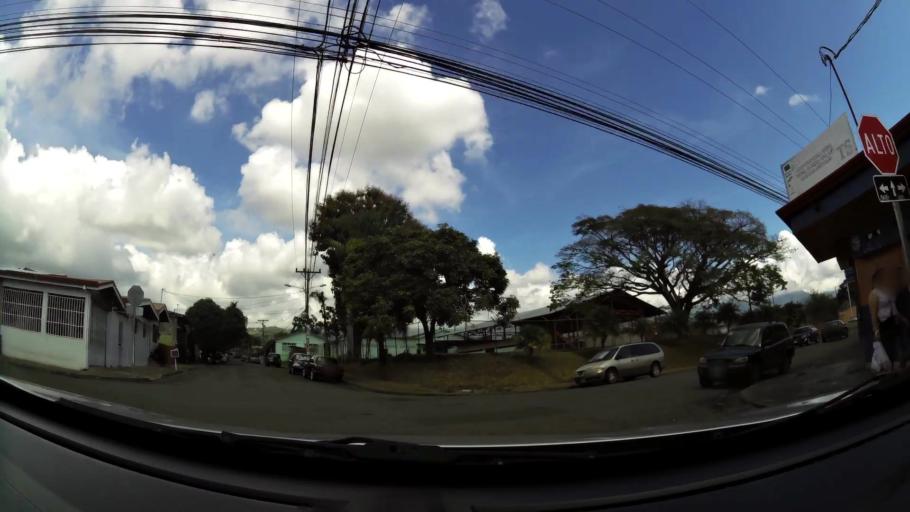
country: CR
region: San Jose
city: San Isidro
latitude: 9.3778
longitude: -83.7051
